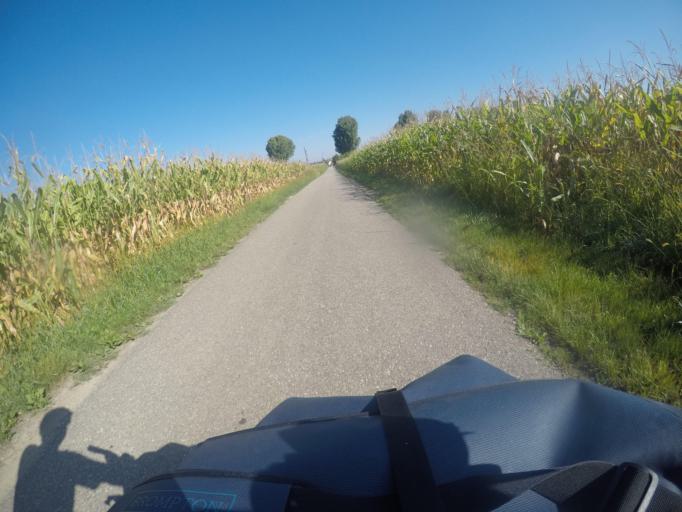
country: FR
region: Alsace
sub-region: Departement du Haut-Rhin
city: Ottmarsheim
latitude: 47.7822
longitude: 7.5056
